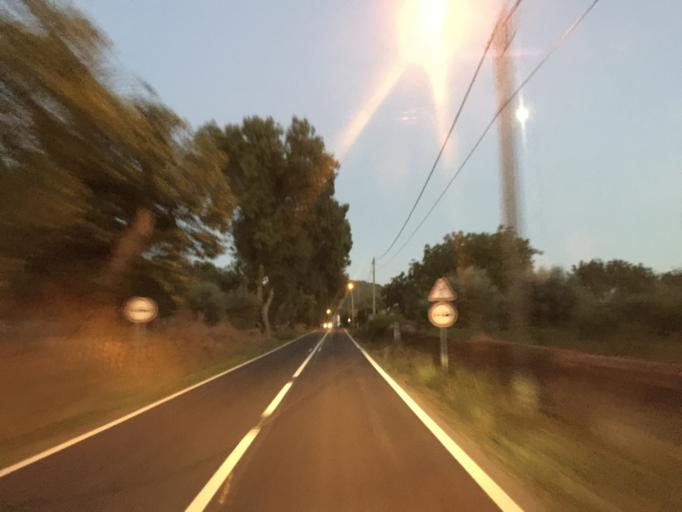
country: PT
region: Portalegre
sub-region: Marvao
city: Marvao
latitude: 39.3891
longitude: -7.4080
